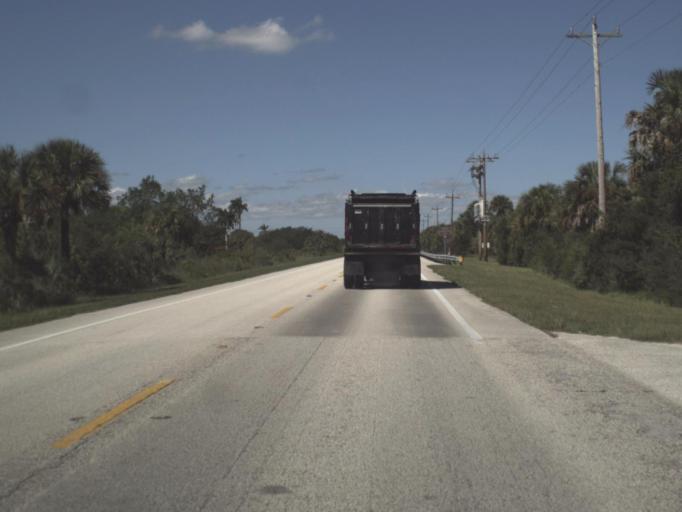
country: US
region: Florida
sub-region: Collier County
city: Marco
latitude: 25.9401
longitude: -81.4660
